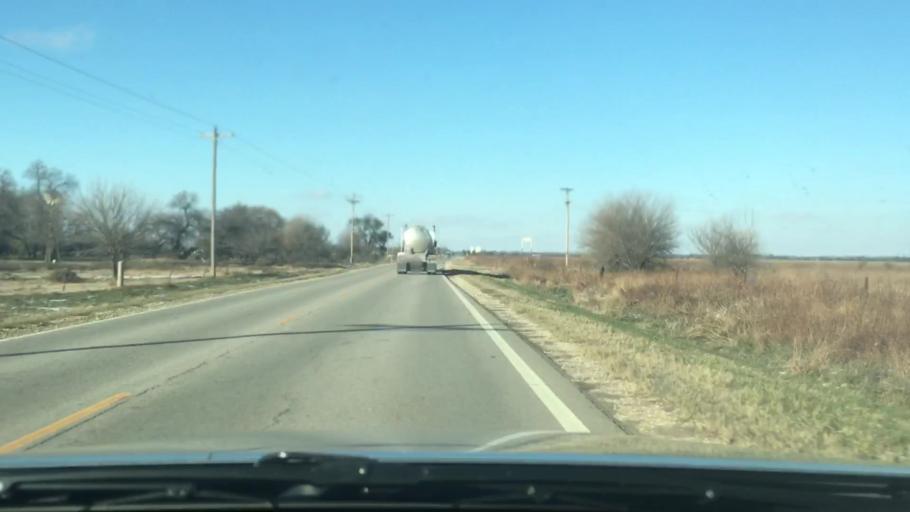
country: US
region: Kansas
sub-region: Rice County
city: Sterling
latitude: 38.1726
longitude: -98.2069
